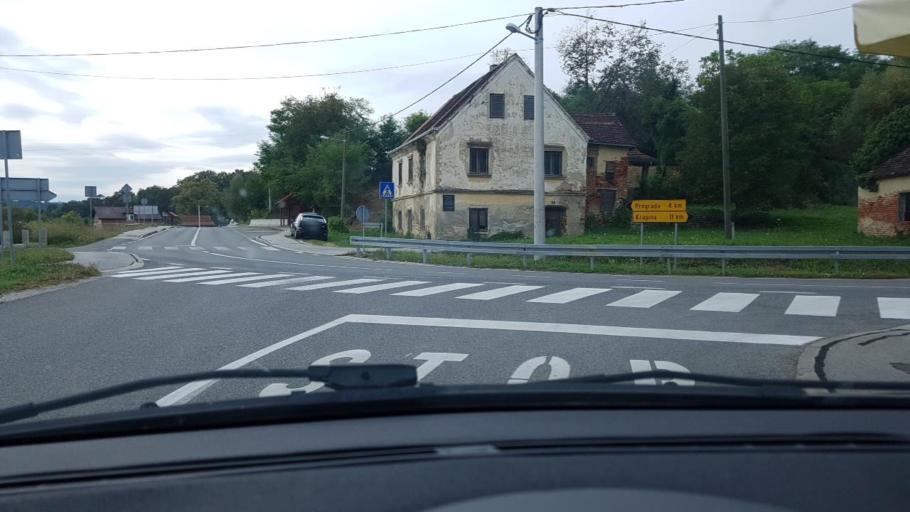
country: HR
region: Krapinsko-Zagorska
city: Pregrada
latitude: 46.1425
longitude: 15.7895
